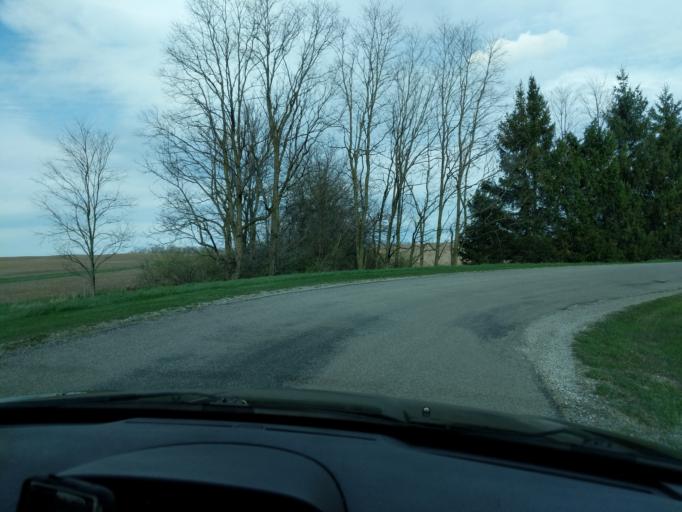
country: US
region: Ohio
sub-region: Champaign County
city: North Lewisburg
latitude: 40.1913
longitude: -83.6464
